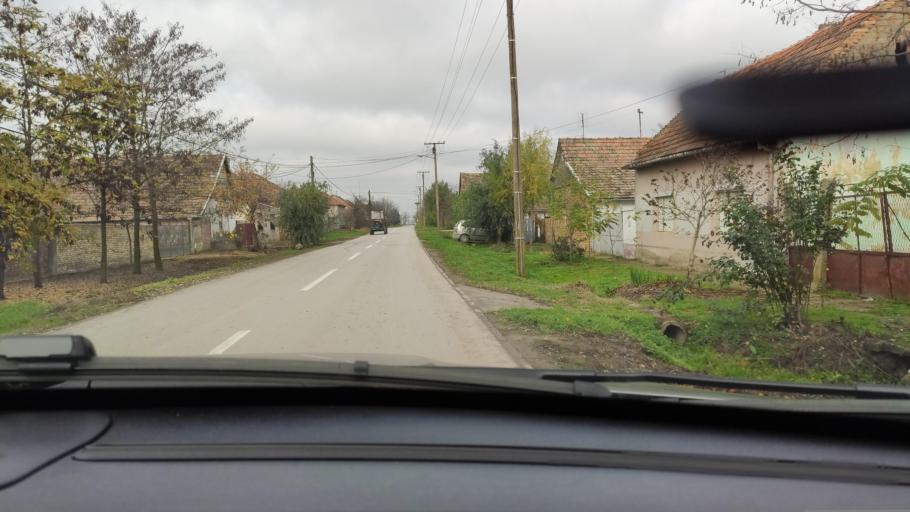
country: RS
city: Jazovo
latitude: 45.9009
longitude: 20.2170
